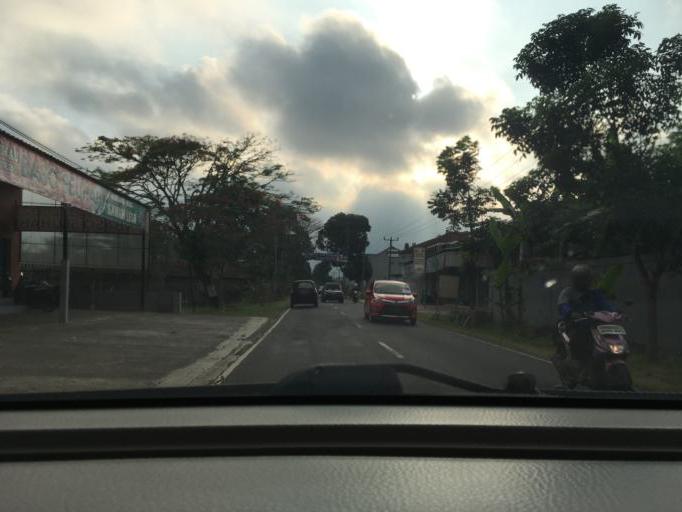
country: ID
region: West Java
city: Kasturi
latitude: -7.0234
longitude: 108.3541
